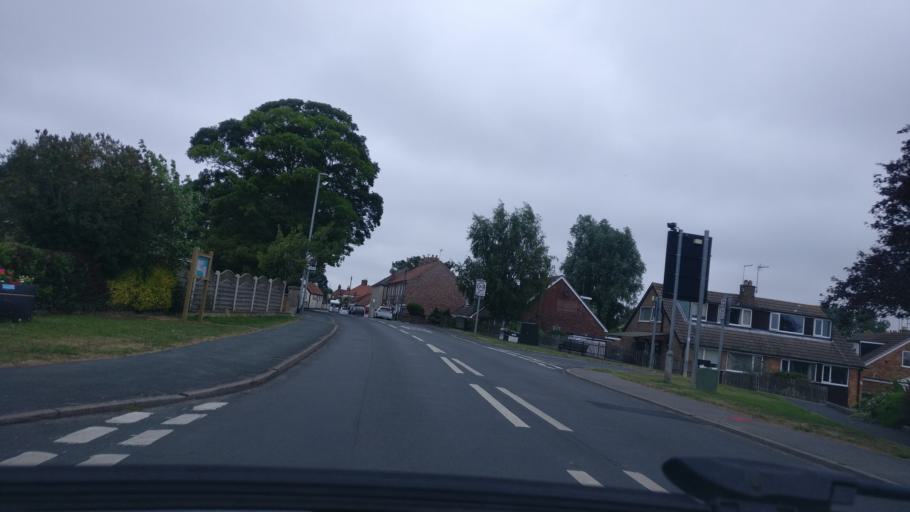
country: GB
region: England
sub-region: East Riding of Yorkshire
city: Leven
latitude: 53.8909
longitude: -0.3166
